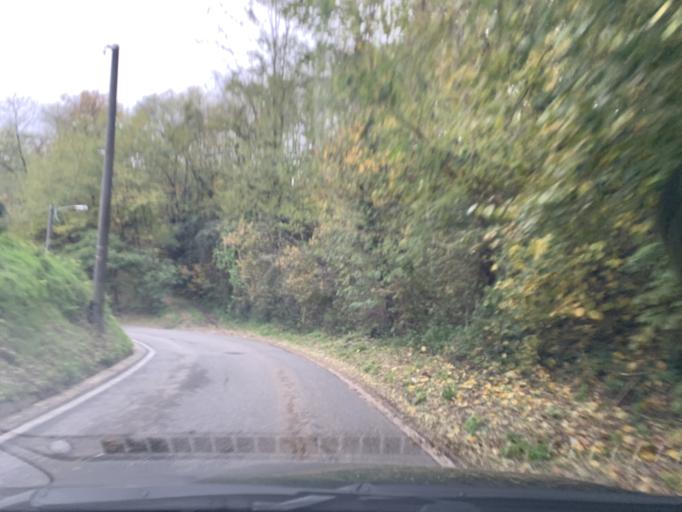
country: IT
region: Lombardy
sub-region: Provincia di Como
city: Casnate Con Bernate
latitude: 45.7469
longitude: 9.0696
